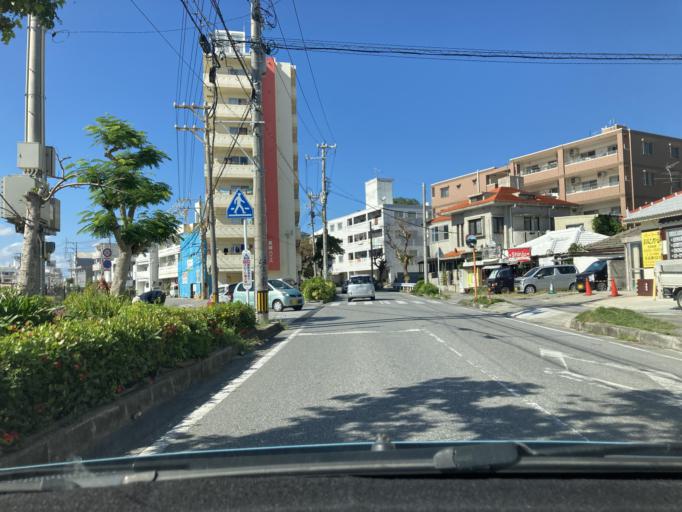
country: JP
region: Okinawa
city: Naha-shi
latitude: 26.2391
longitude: 127.6971
